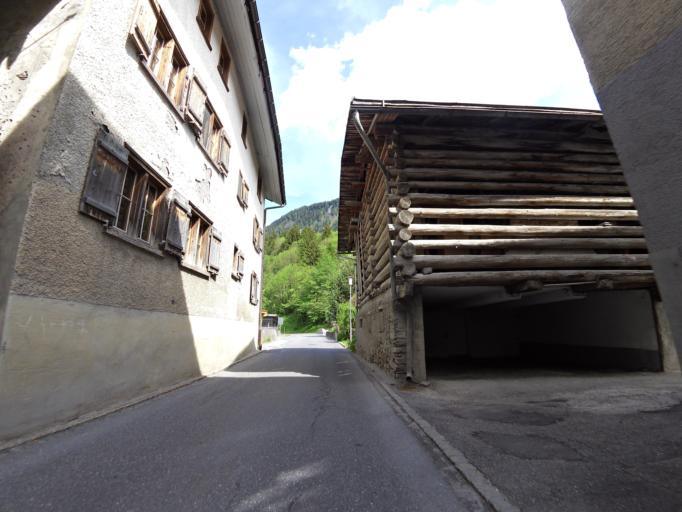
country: CH
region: Grisons
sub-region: Surselva District
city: Ilanz
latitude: 46.7756
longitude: 9.2327
